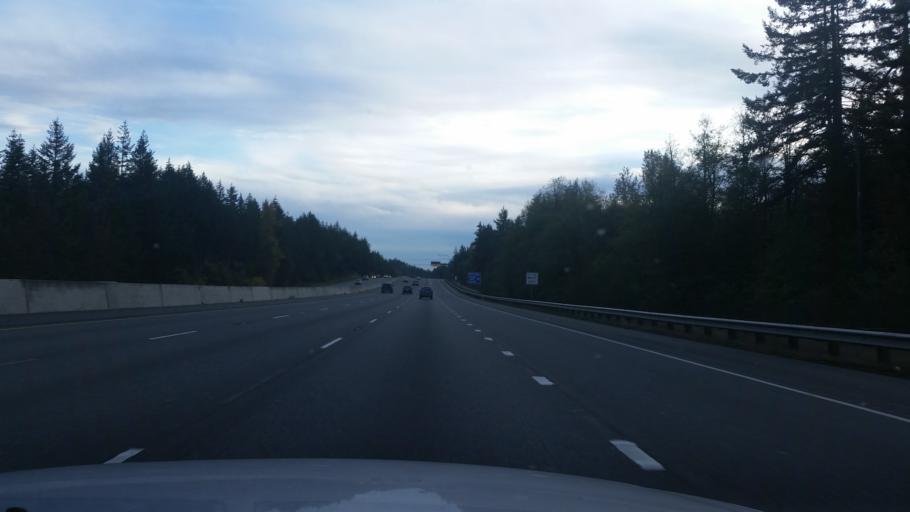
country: US
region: Washington
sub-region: Thurston County
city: Grand Mound
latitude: 46.8778
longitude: -122.9671
